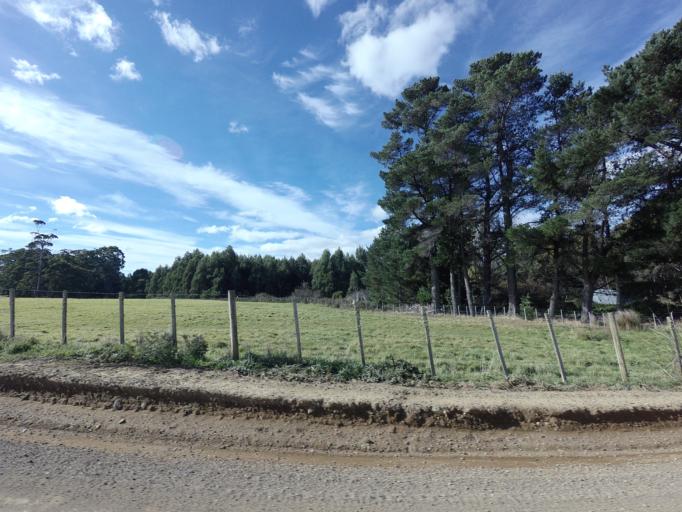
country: AU
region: Tasmania
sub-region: Clarence
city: Sandford
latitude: -43.1576
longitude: 147.7667
